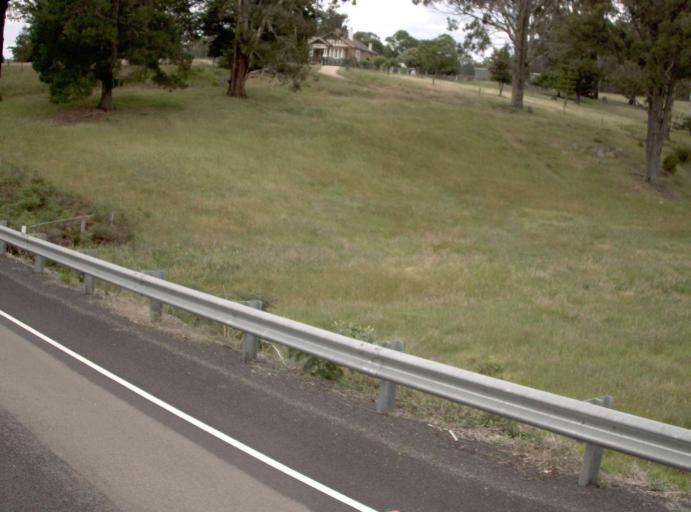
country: AU
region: New South Wales
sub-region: Bombala
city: Bombala
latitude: -37.4845
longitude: 149.1806
